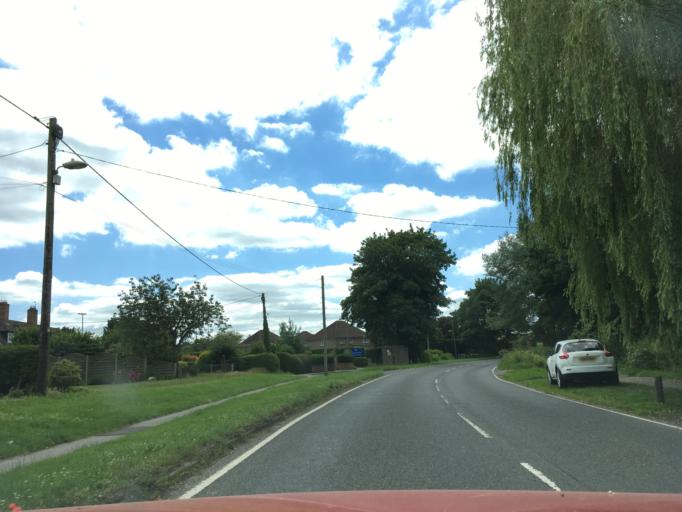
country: GB
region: England
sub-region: Hampshire
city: Overton
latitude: 51.2246
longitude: -1.3376
